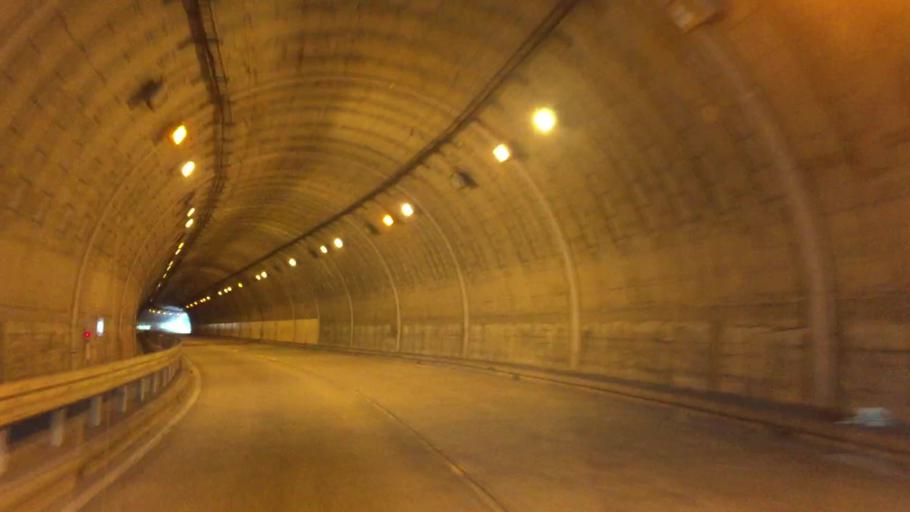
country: JP
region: Kanagawa
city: Zushi
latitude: 35.3593
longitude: 139.6064
